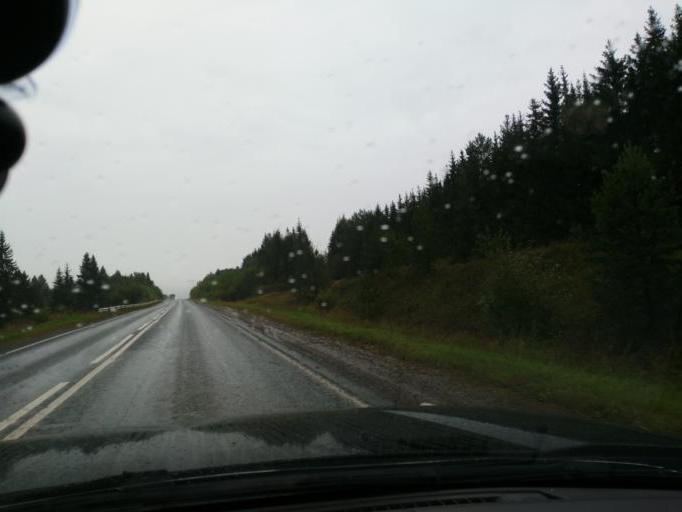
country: RU
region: Perm
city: Yugo-Kamskiy
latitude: 57.5766
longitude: 55.6813
